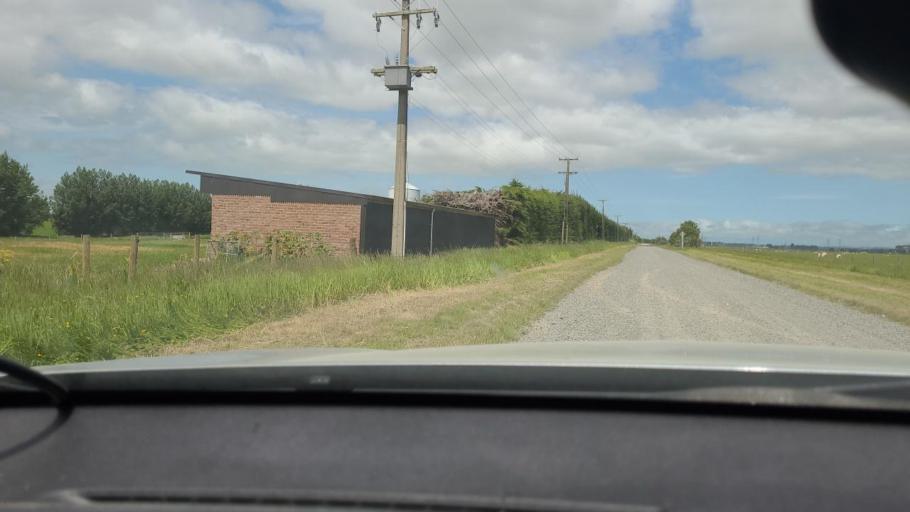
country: NZ
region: Southland
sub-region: Southland District
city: Winton
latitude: -46.0299
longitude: 168.0553
